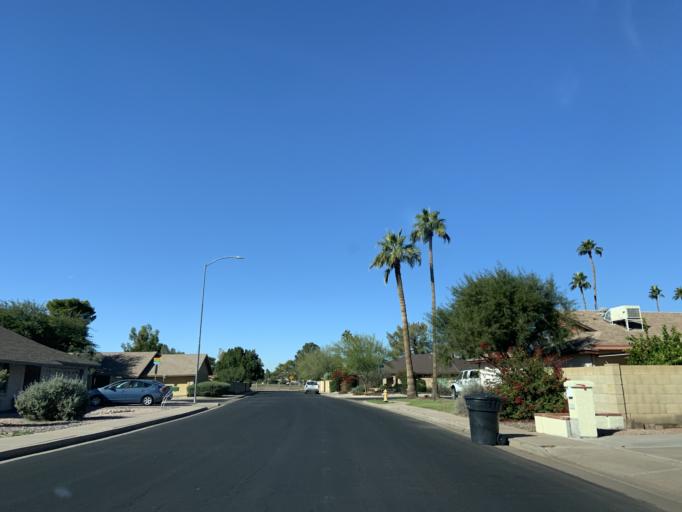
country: US
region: Arizona
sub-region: Maricopa County
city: San Carlos
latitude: 33.3673
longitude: -111.8639
